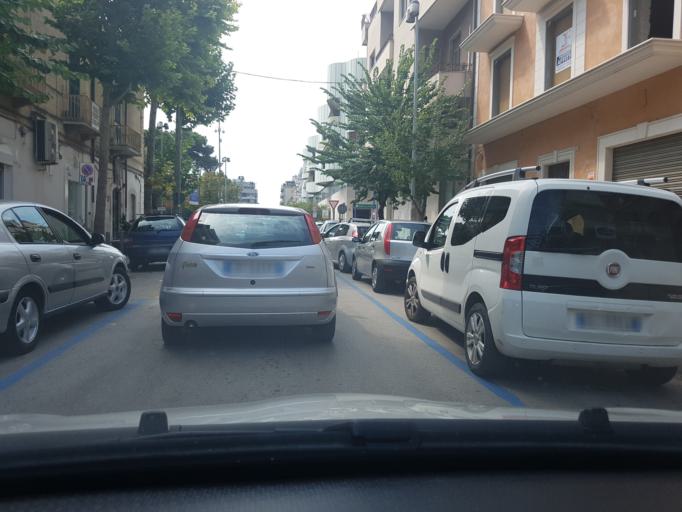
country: IT
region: Apulia
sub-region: Provincia di Foggia
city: Cerignola
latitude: 41.2649
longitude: 15.9032
